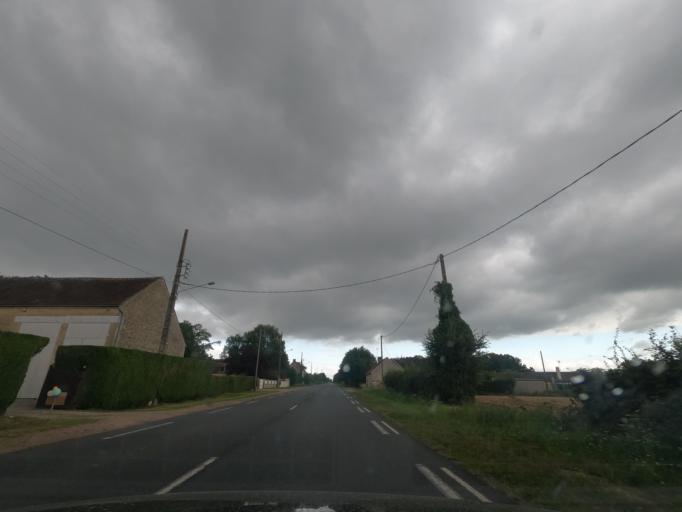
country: FR
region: Lower Normandy
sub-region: Departement de l'Orne
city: Trun
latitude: 48.7580
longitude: 0.0801
